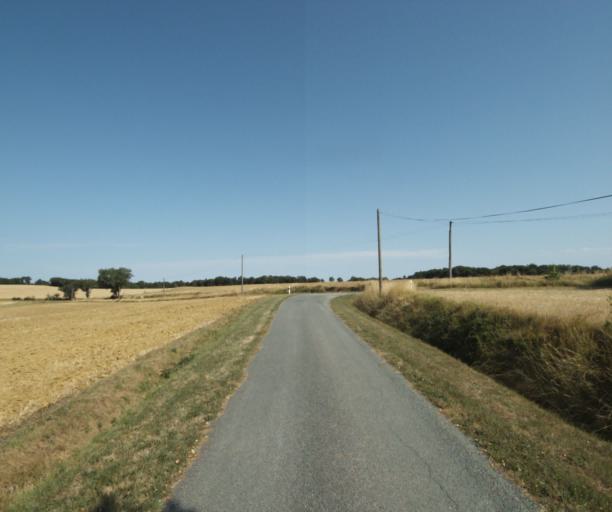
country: FR
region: Midi-Pyrenees
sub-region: Departement de la Haute-Garonne
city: Saint-Felix-Lauragais
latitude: 43.4259
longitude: 1.8414
